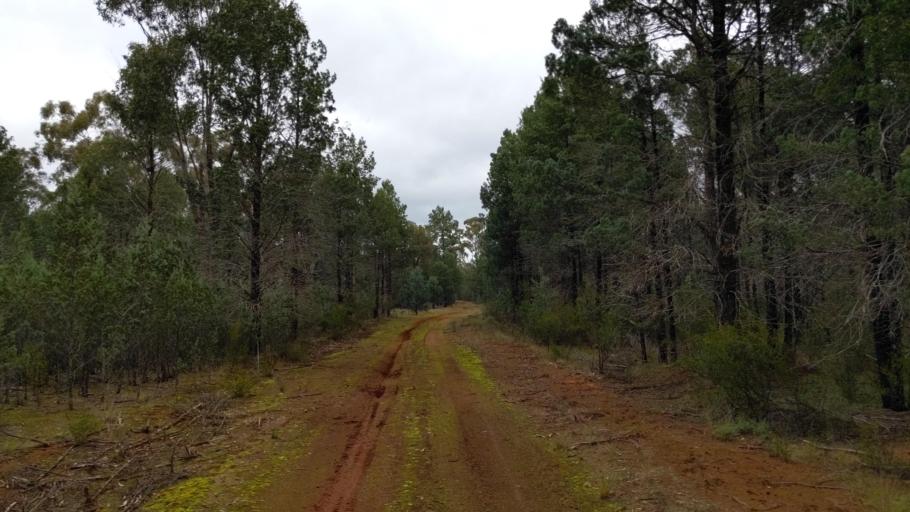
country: AU
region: New South Wales
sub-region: Coolamon
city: Coolamon
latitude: -34.8463
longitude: 146.9327
